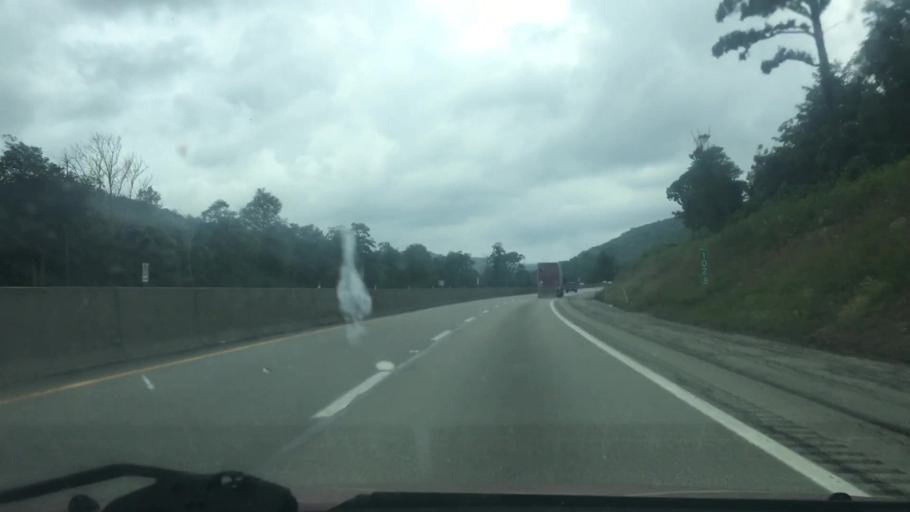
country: US
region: Pennsylvania
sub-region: Somerset County
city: Somerset
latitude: 40.0779
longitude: -79.1823
